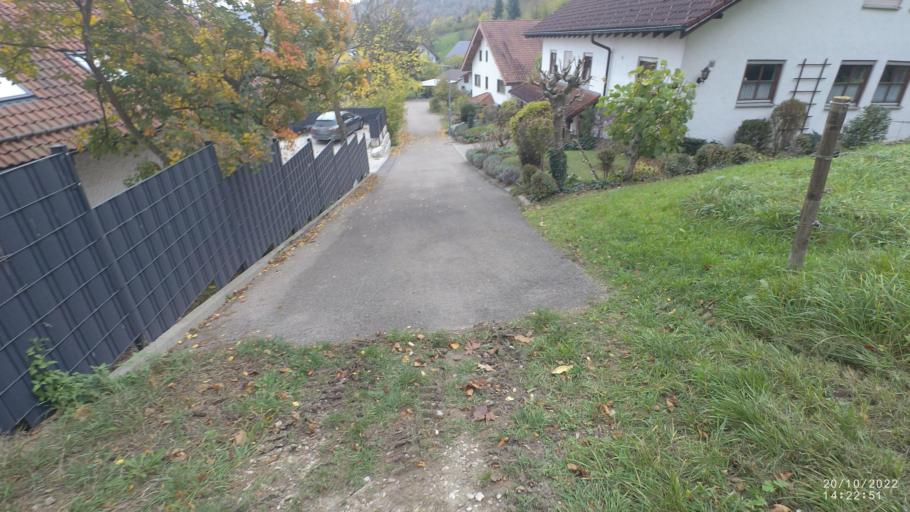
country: DE
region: Baden-Wuerttemberg
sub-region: Regierungsbezirk Stuttgart
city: Muhlhausen
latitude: 48.5823
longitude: 9.6540
